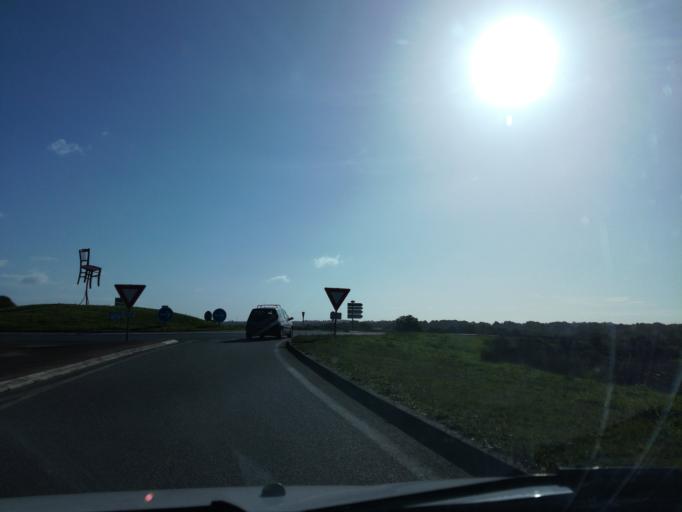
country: FR
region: Pays de la Loire
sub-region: Departement de Maine-et-Loire
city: Pouance
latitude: 47.7610
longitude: -1.2048
